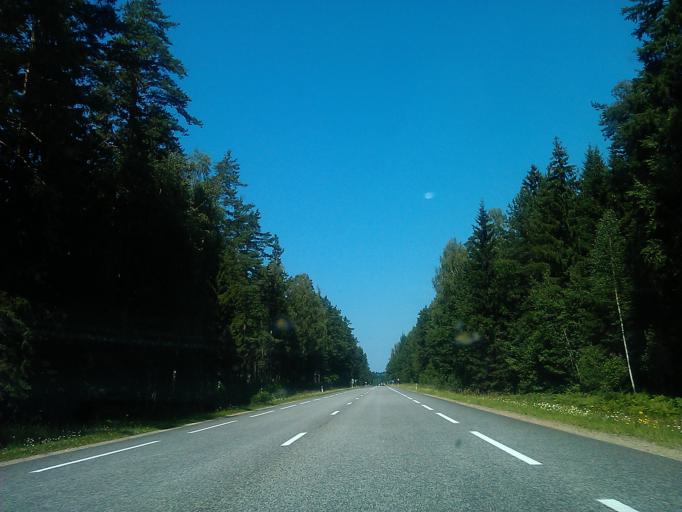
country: LV
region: Saulkrastu
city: Saulkrasti
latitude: 57.3751
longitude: 24.4338
